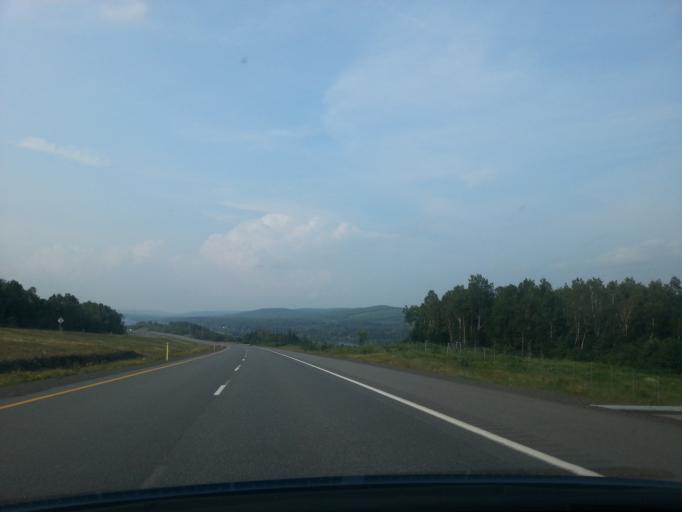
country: US
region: Maine
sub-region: Aroostook County
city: Fort Fairfield
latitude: 46.6603
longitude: -67.7319
